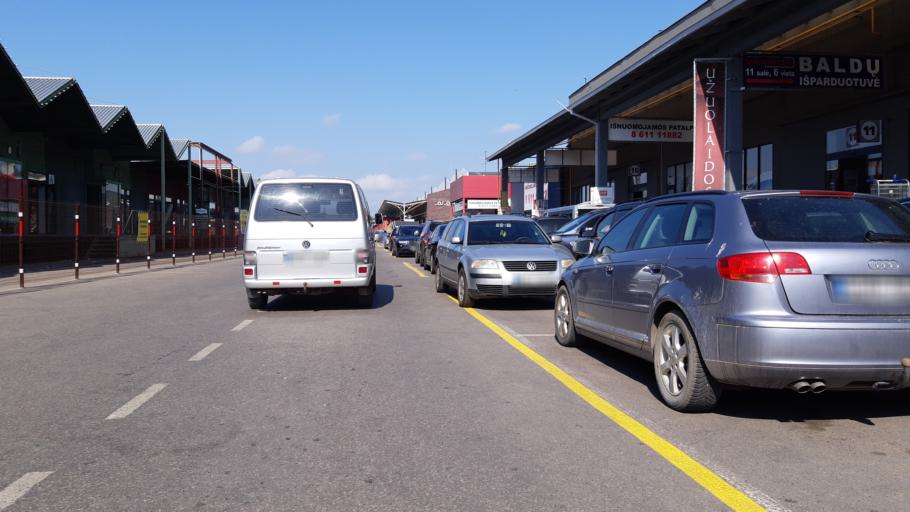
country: LT
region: Kauno apskritis
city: Dainava (Kaunas)
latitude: 54.9155
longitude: 23.9936
